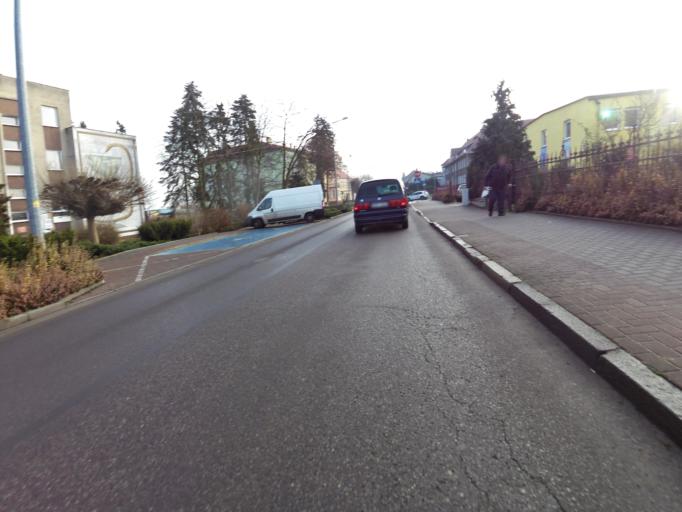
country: PL
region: West Pomeranian Voivodeship
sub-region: Powiat mysliborski
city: Debno
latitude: 52.7361
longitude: 14.7017
